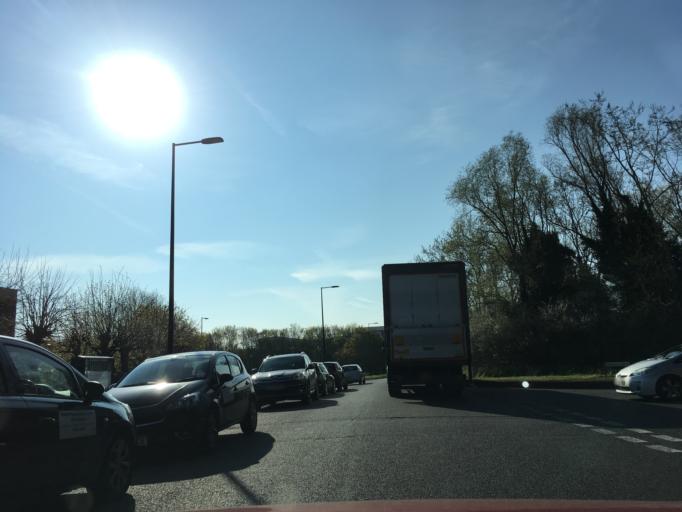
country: GB
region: England
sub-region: Milton Keynes
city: Newport Pagnell
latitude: 52.0684
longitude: -0.7305
